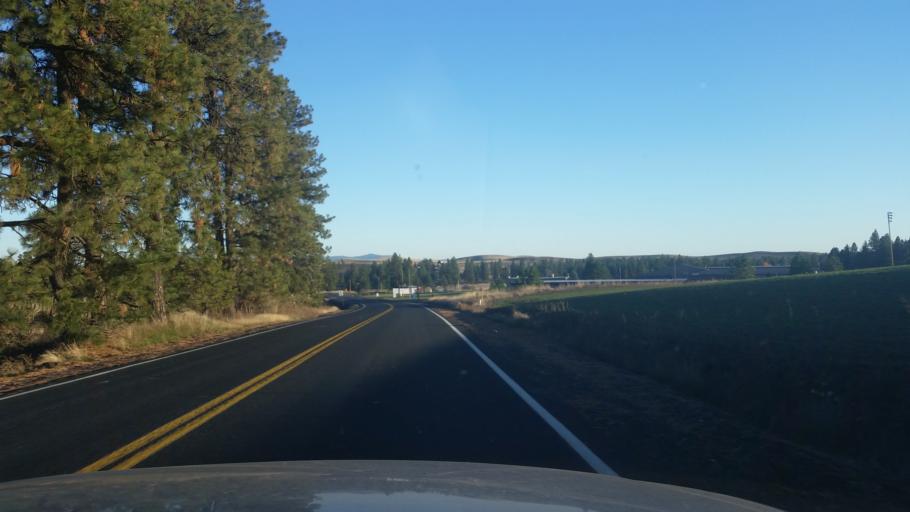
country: US
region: Washington
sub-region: Spokane County
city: Cheney
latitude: 47.3862
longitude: -117.3211
